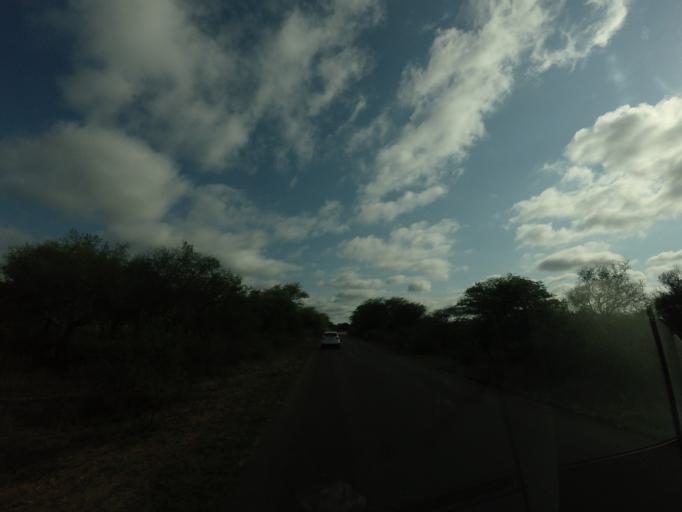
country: ZA
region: Mpumalanga
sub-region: Ehlanzeni District
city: Komatipoort
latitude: -25.2178
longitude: 31.8651
